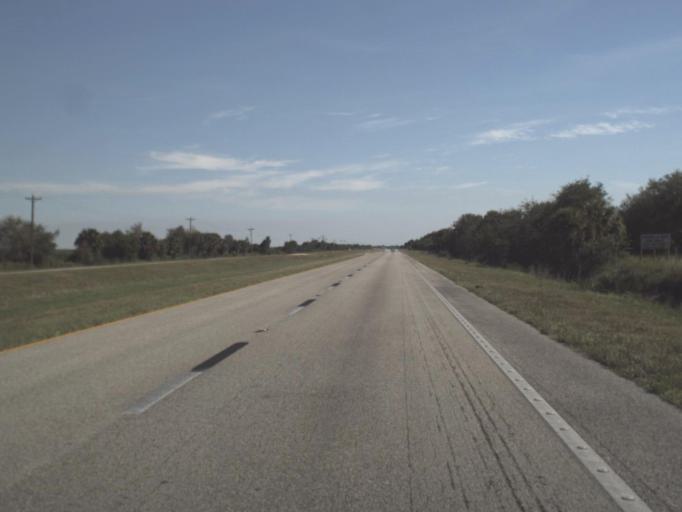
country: US
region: Florida
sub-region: Glades County
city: Moore Haven
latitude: 26.8544
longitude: -81.2070
